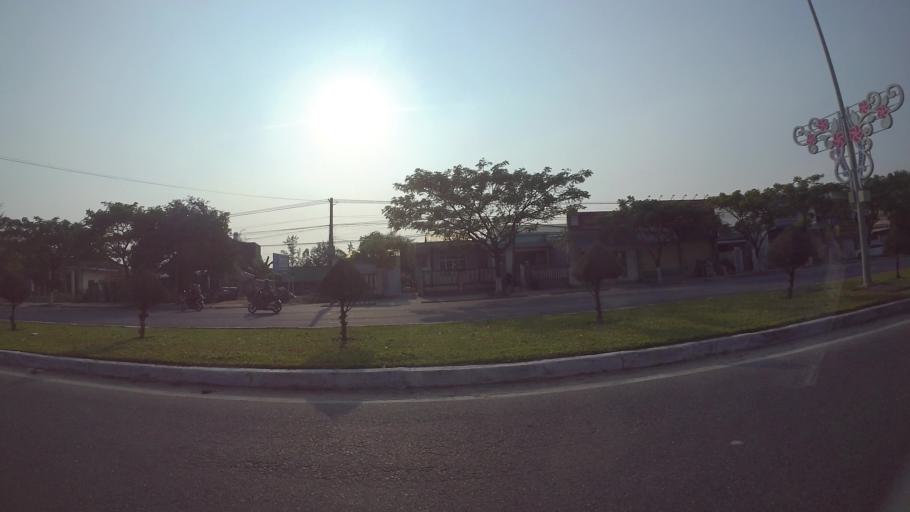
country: VN
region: Da Nang
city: Ngu Hanh Son
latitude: 15.9623
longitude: 108.2548
